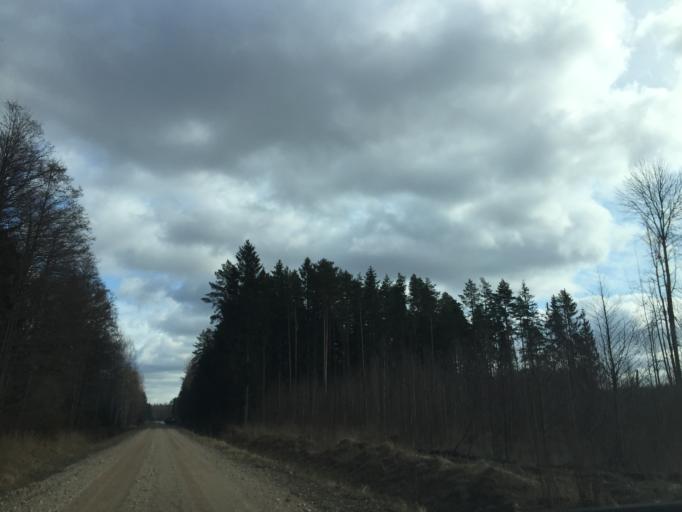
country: LV
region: Vecumnieki
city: Vecumnieki
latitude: 56.5894
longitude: 24.6442
